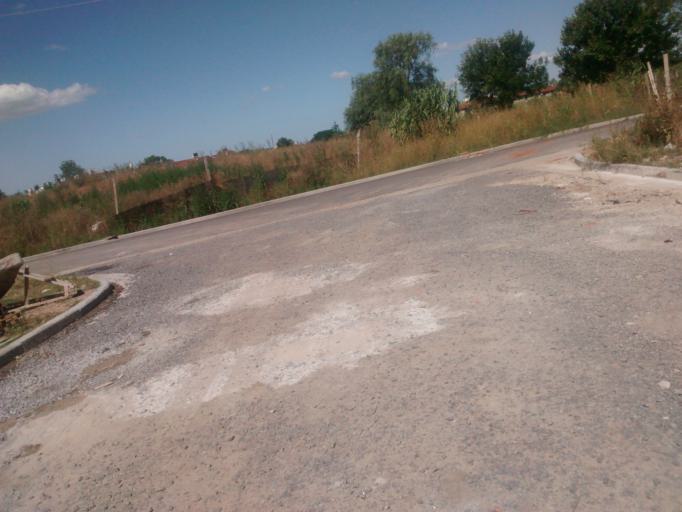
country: AR
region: Buenos Aires
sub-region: Partido de La Plata
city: La Plata
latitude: -34.9344
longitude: -57.9080
